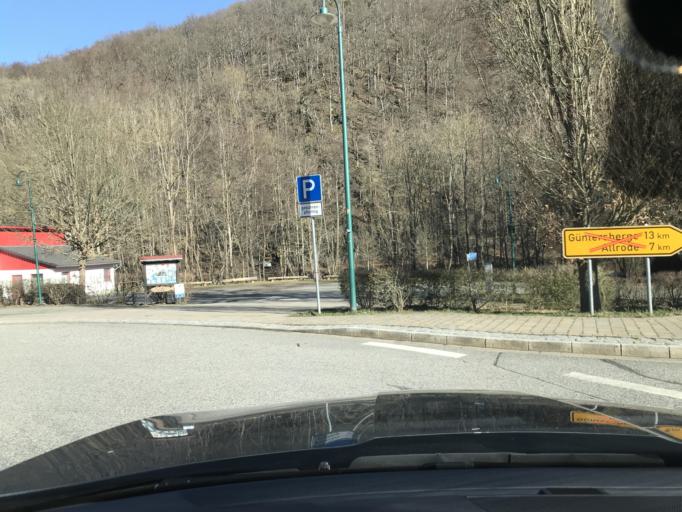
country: DE
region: Saxony-Anhalt
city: Timmenrode
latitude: 51.7160
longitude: 10.9741
